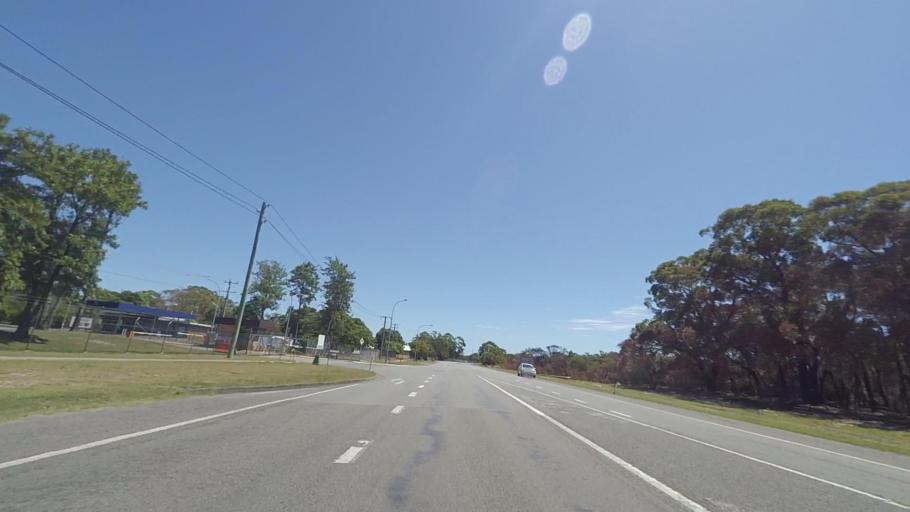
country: AU
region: New South Wales
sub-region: Port Stephens Shire
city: Medowie
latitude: -32.7943
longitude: 151.8530
